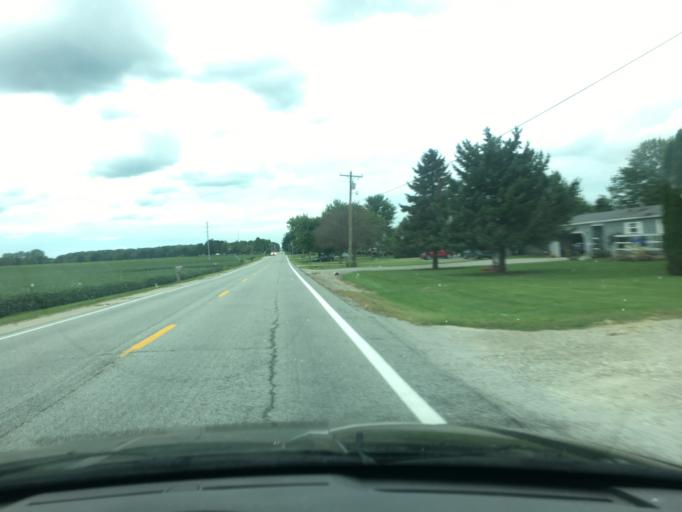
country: US
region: Ohio
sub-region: Champaign County
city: Urbana
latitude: 40.1510
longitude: -83.6847
